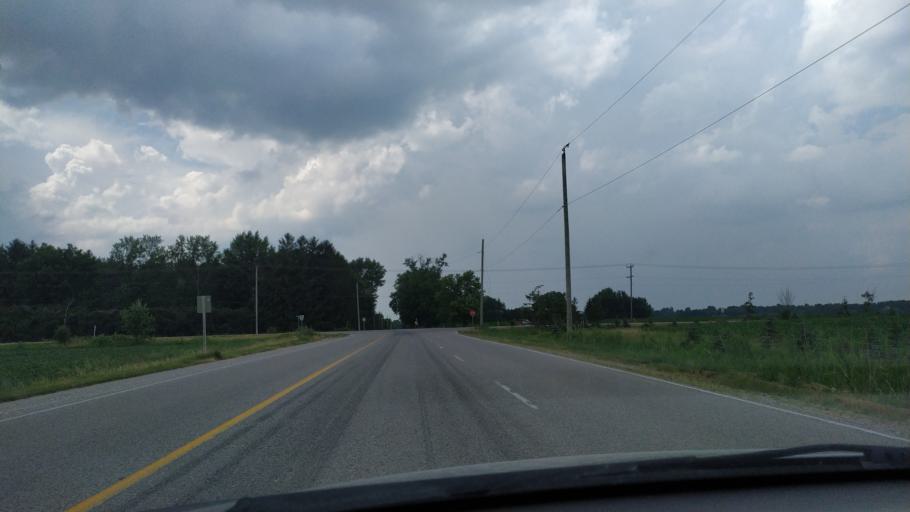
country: CA
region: Ontario
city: London
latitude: 43.1517
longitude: -81.1824
